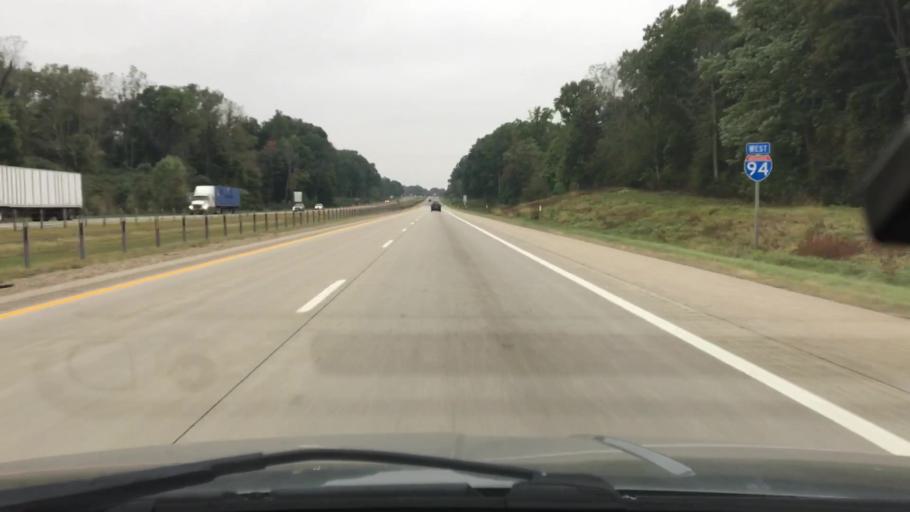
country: US
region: Michigan
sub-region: Van Buren County
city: Paw Paw
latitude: 42.1966
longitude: -85.9762
